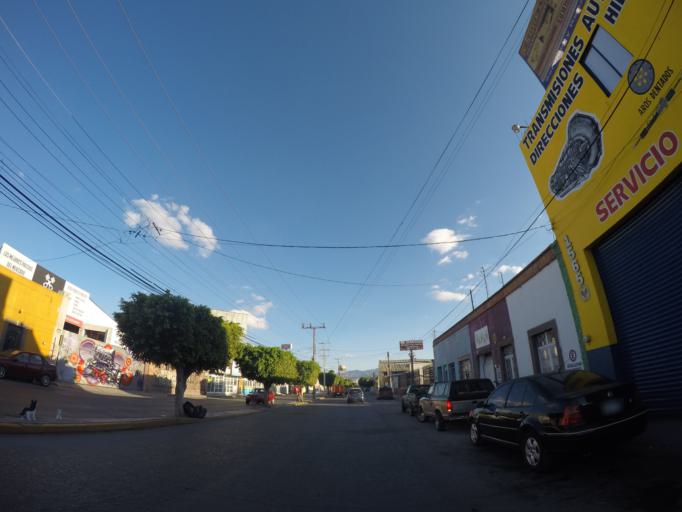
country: MX
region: San Luis Potosi
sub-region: San Luis Potosi
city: San Luis Potosi
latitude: 22.1669
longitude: -100.9807
